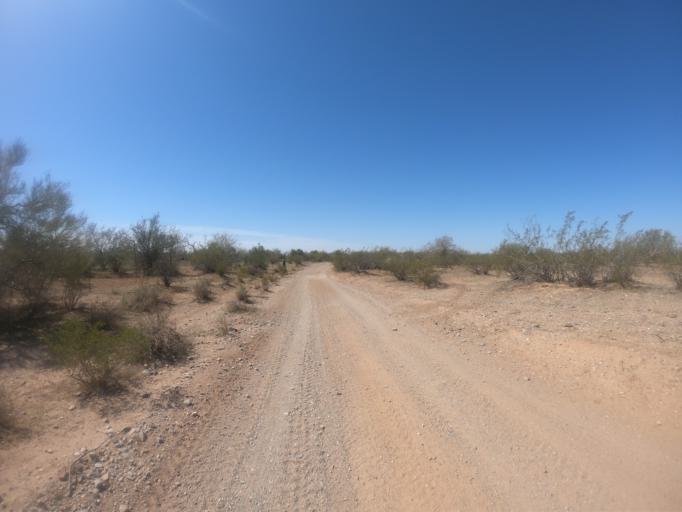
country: US
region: Arizona
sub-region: Pinal County
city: Gold Camp
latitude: 33.2416
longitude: -111.3270
